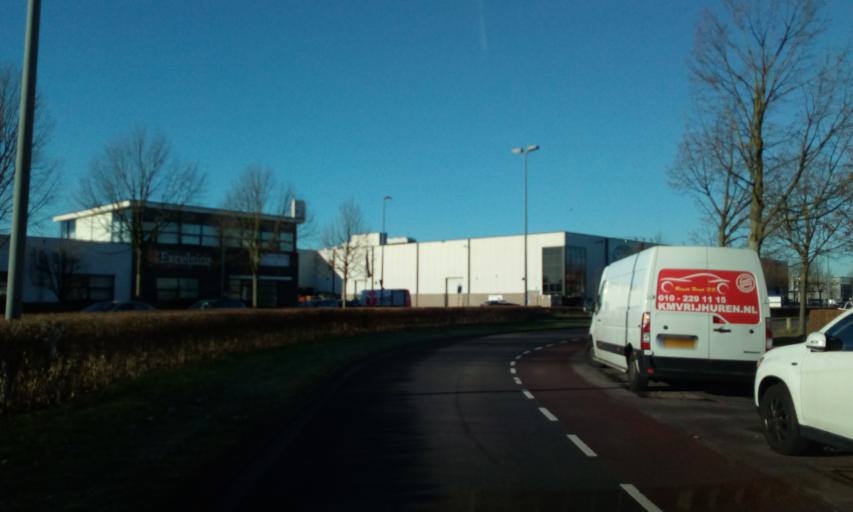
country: NL
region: South Holland
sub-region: Gemeente Leidschendam-Voorburg
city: Voorburg
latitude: 52.0674
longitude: 4.3928
